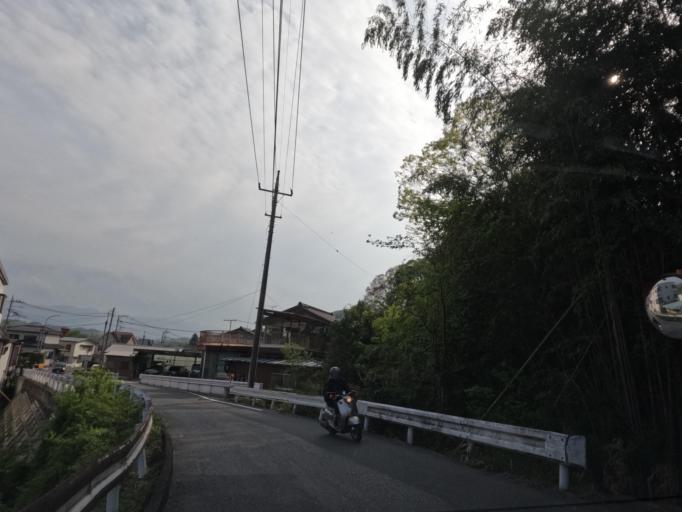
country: JP
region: Saitama
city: Chichibu
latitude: 36.0800
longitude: 139.0930
